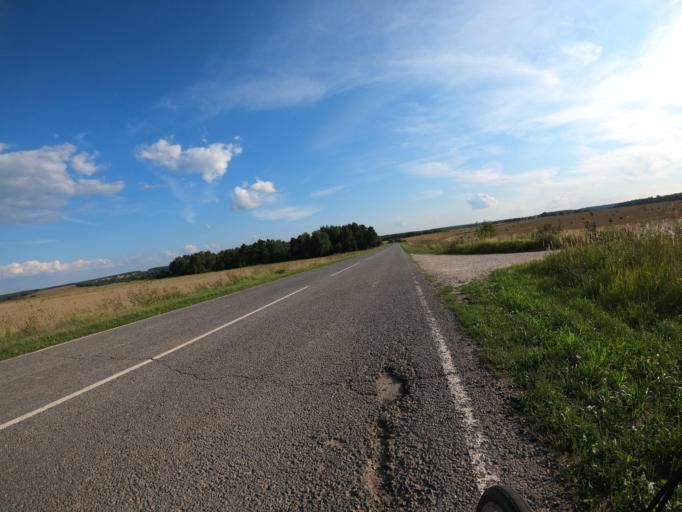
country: RU
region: Moskovskaya
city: Meshcherino
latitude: 55.1569
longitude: 38.4329
